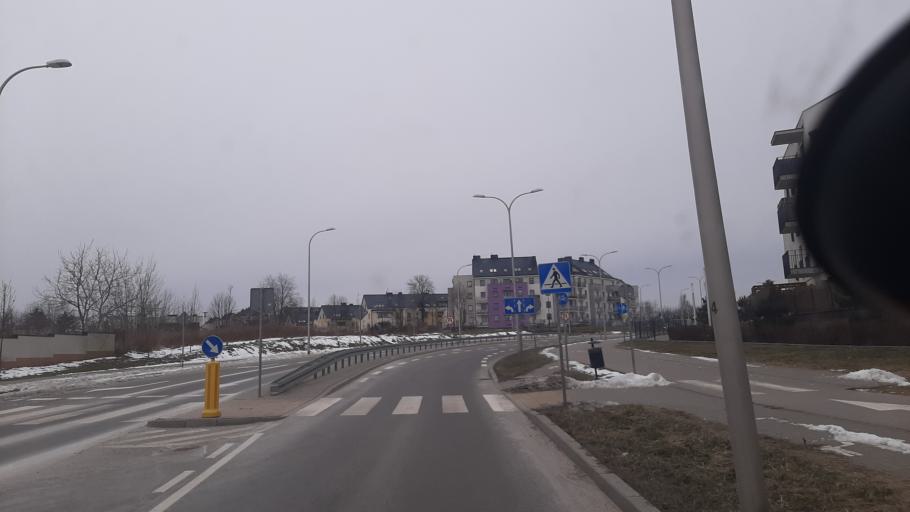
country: PL
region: Lublin Voivodeship
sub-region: Powiat lubelski
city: Lublin
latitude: 51.2733
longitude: 22.5812
